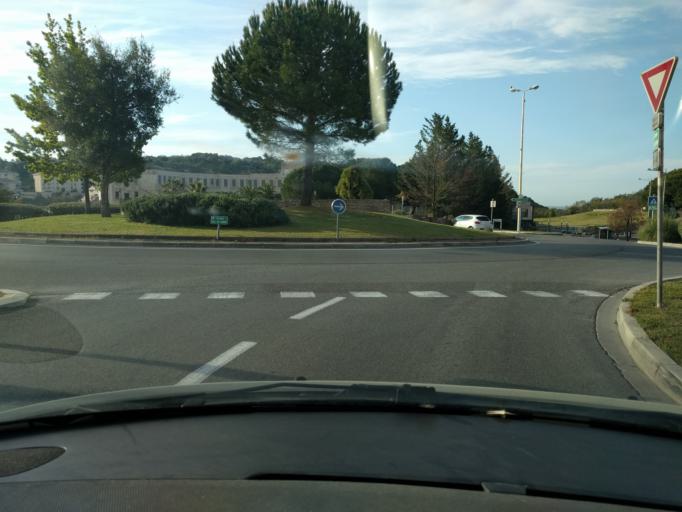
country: FR
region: Provence-Alpes-Cote d'Azur
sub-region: Departement des Alpes-Maritimes
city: Cannes
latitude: 43.5675
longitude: 6.9810
